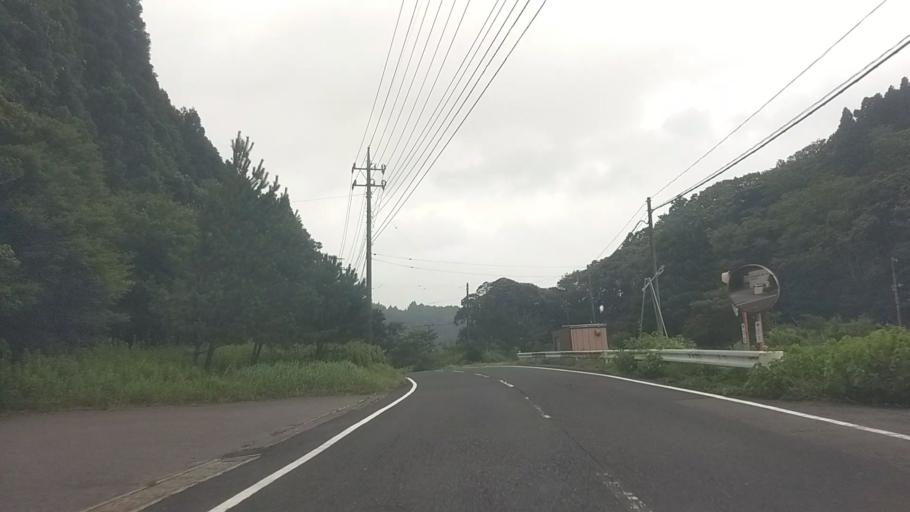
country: JP
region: Chiba
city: Katsuura
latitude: 35.2525
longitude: 140.2447
